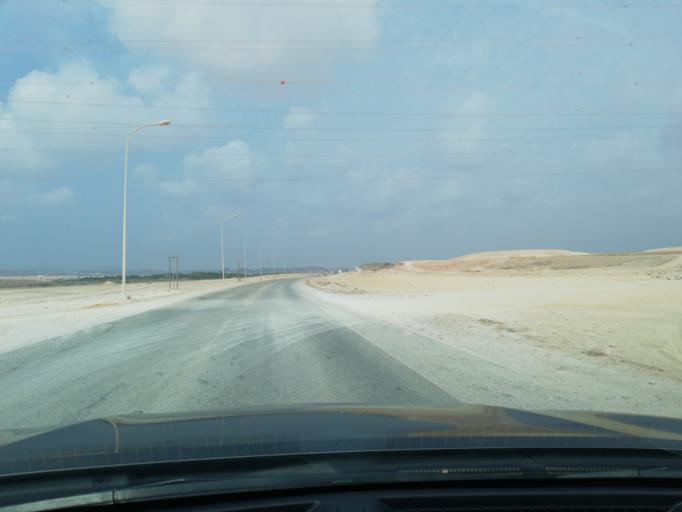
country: OM
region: Zufar
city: Salalah
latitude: 16.9470
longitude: 53.9597
